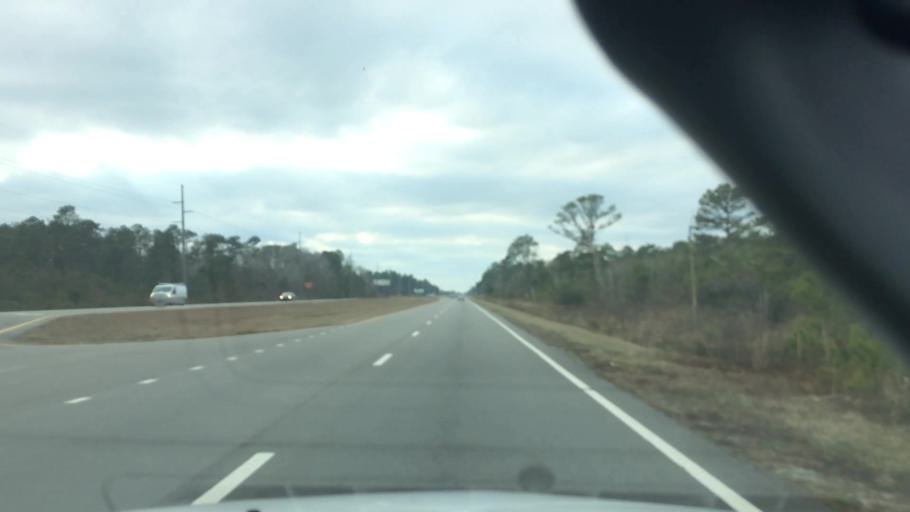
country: US
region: North Carolina
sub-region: Brunswick County
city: Sunset Beach
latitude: 33.9435
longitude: -78.5223
